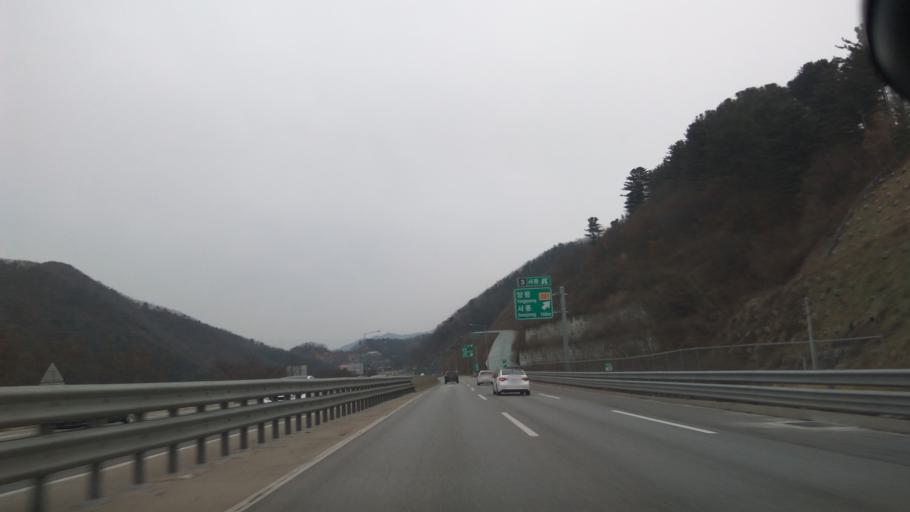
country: KR
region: Gyeonggi-do
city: Hwado
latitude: 37.6338
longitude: 127.3637
